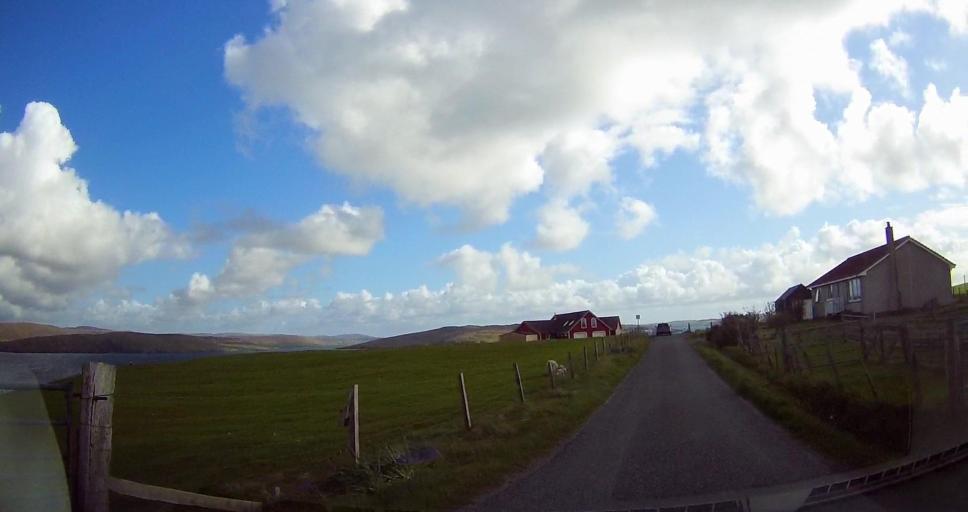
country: GB
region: Scotland
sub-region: Shetland Islands
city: Lerwick
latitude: 60.3604
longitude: -1.3834
